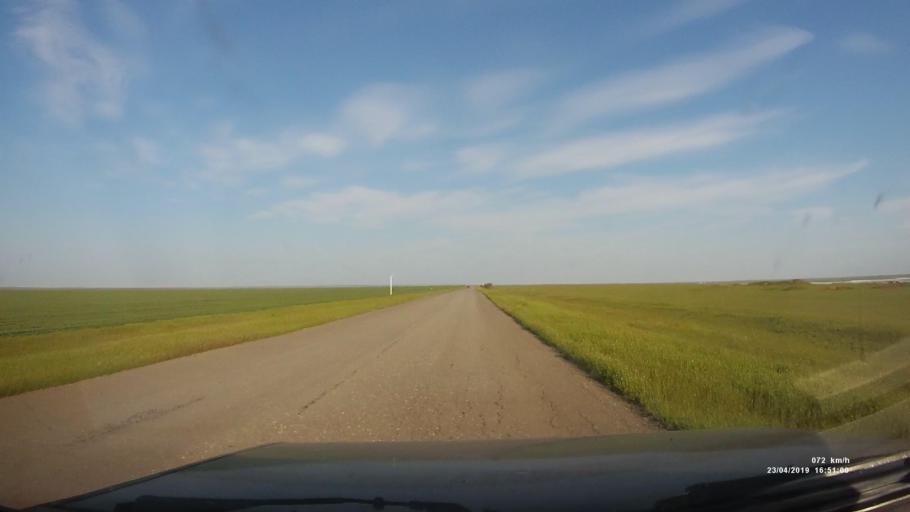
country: RU
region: Kalmykiya
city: Priyutnoye
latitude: 46.3248
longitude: 43.2999
